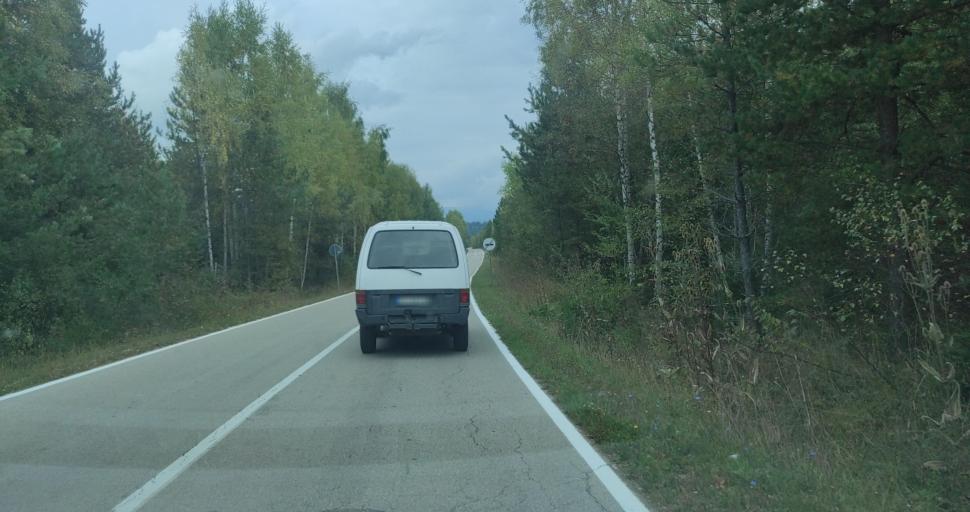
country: RS
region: Central Serbia
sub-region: Jablanicki Okrug
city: Crna Trava
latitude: 42.6845
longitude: 22.3143
